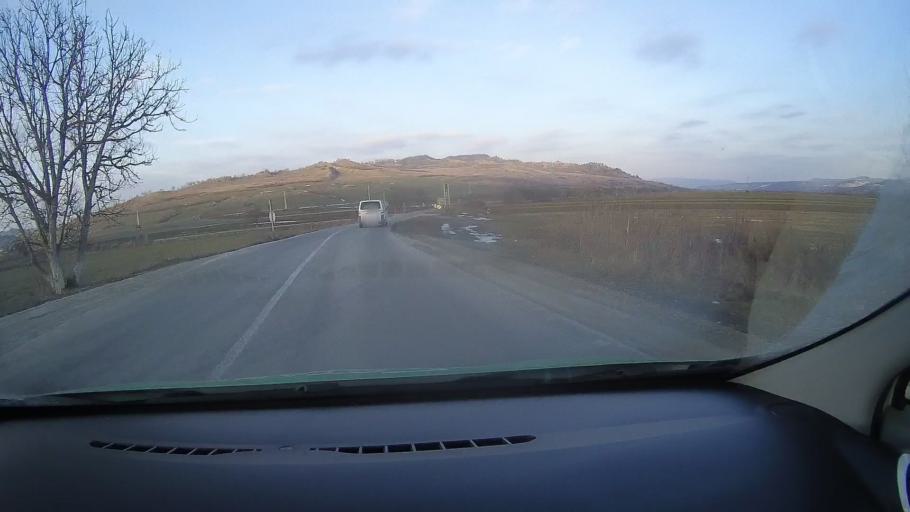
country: RO
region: Mures
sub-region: Comuna Vanatori
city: Vanatori
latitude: 46.2498
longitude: 24.9315
